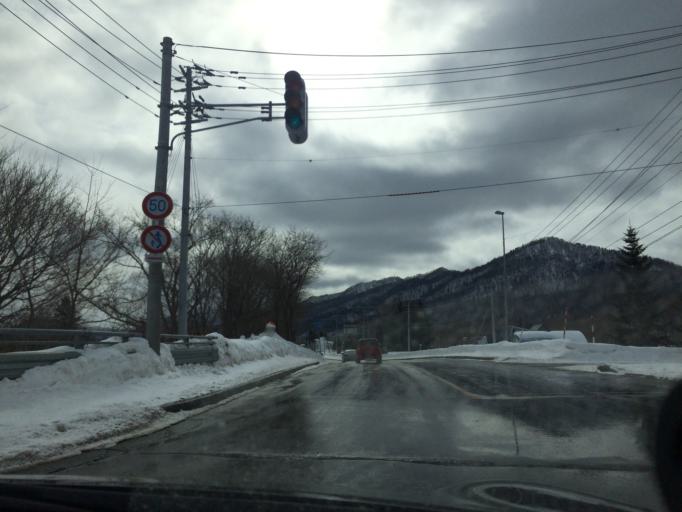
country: JP
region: Hokkaido
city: Iwamizawa
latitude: 42.9779
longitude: 142.0061
